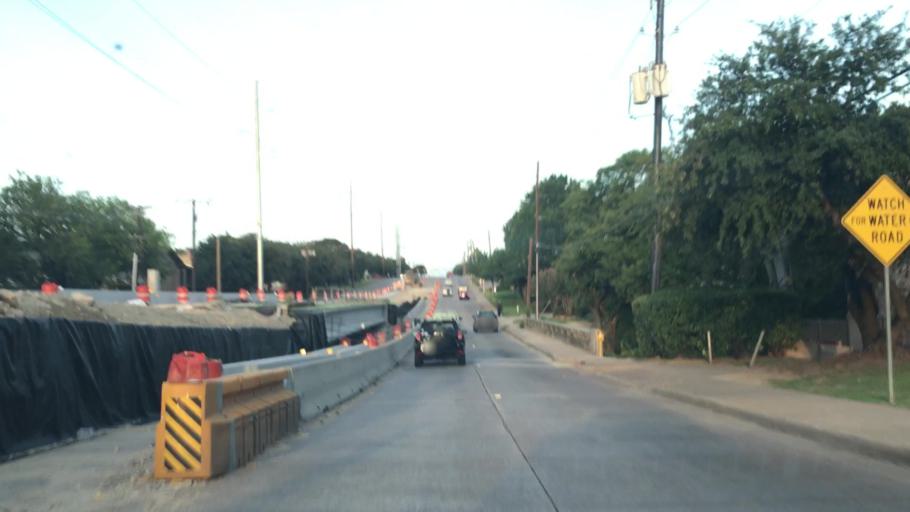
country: US
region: Texas
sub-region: Dallas County
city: Richardson
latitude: 32.9400
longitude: -96.7571
